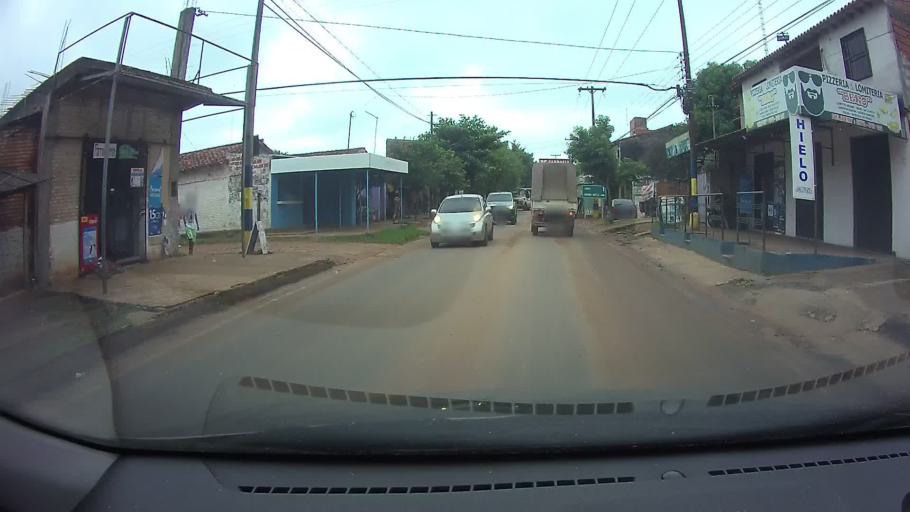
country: PY
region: Central
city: San Lorenzo
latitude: -25.3117
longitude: -57.4913
